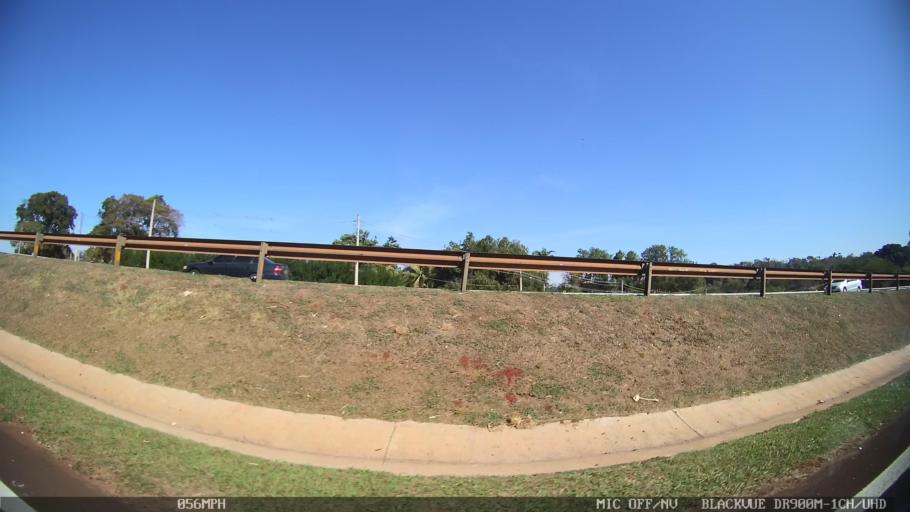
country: BR
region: Sao Paulo
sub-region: Ribeirao Preto
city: Ribeirao Preto
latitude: -21.2167
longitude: -47.8346
